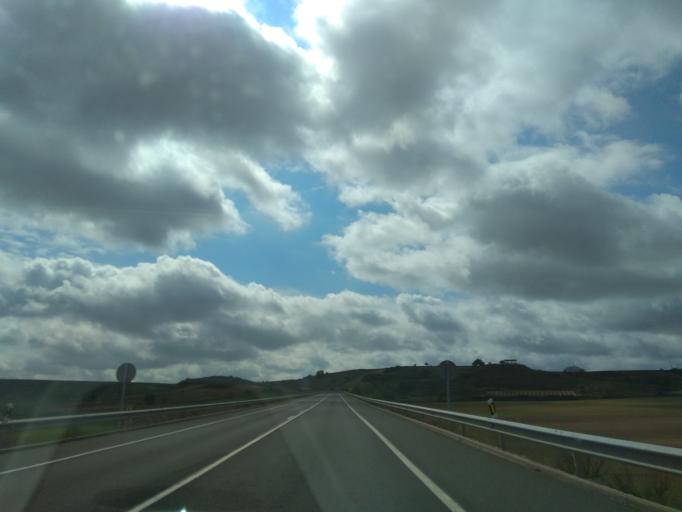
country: ES
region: La Rioja
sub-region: Provincia de La Rioja
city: Casalarreina
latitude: 42.5495
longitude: -2.8921
